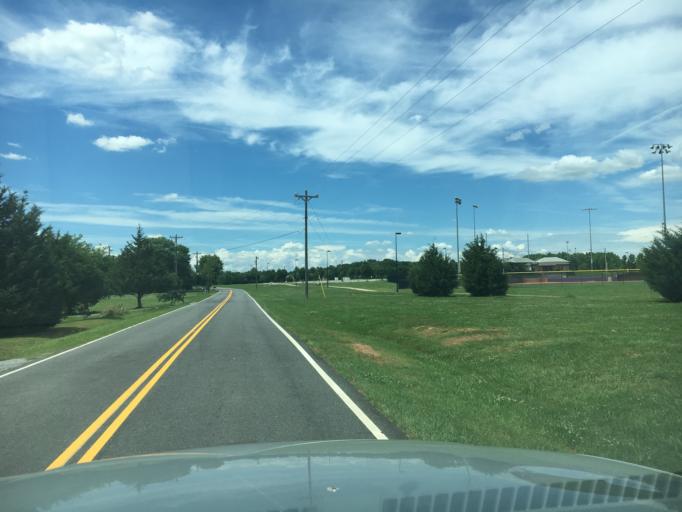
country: US
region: South Carolina
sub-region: Spartanburg County
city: Duncan
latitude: 34.8694
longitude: -82.1068
